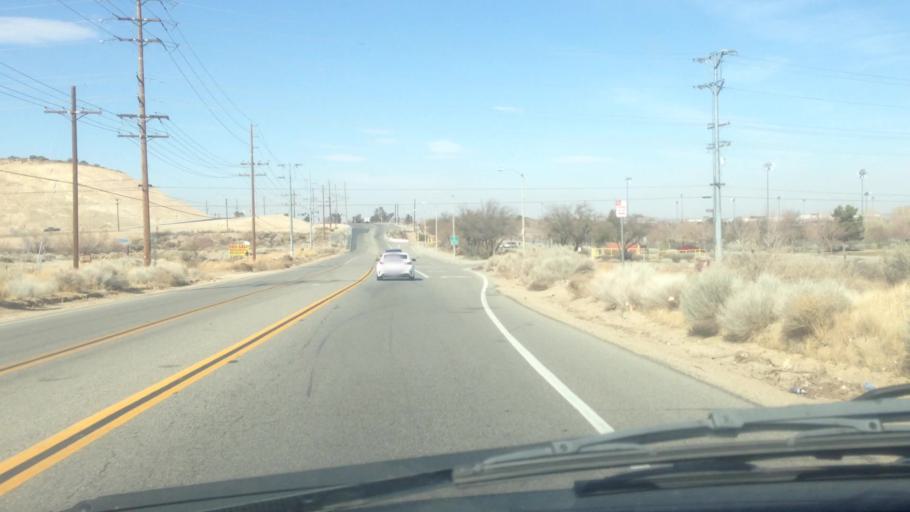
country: US
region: California
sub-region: Los Angeles County
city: Palmdale
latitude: 34.5644
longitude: -118.1402
